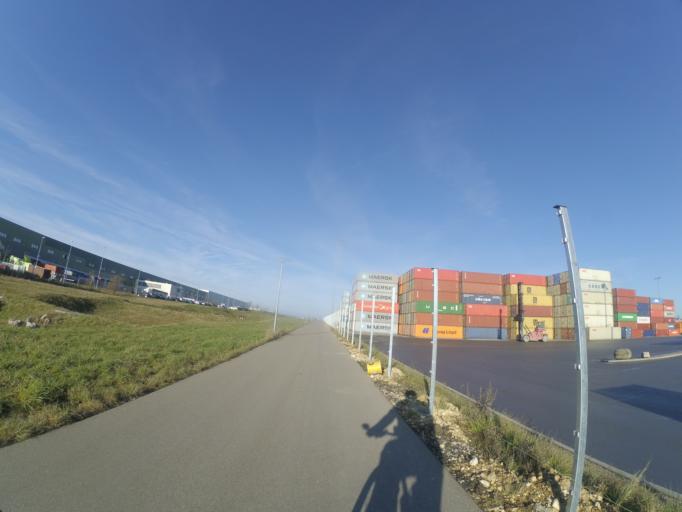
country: DE
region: Baden-Wuerttemberg
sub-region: Tuebingen Region
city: Dornstadt
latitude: 48.4604
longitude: 9.9693
